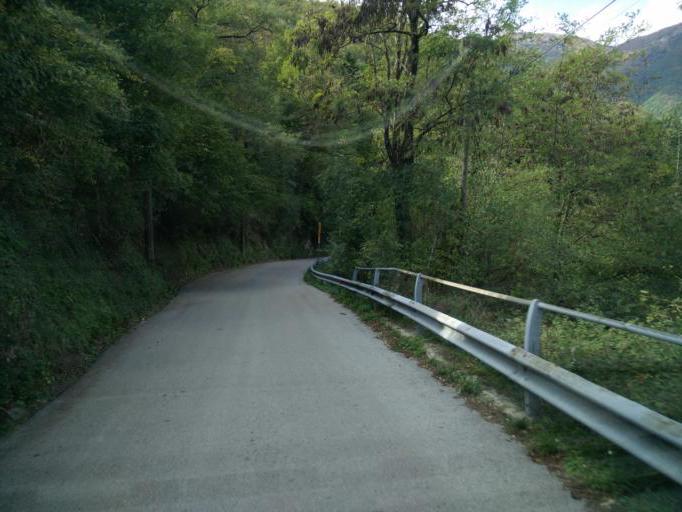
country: IT
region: Liguria
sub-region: Provincia di La Spezia
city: Sesta Godano
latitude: 44.3374
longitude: 9.7015
